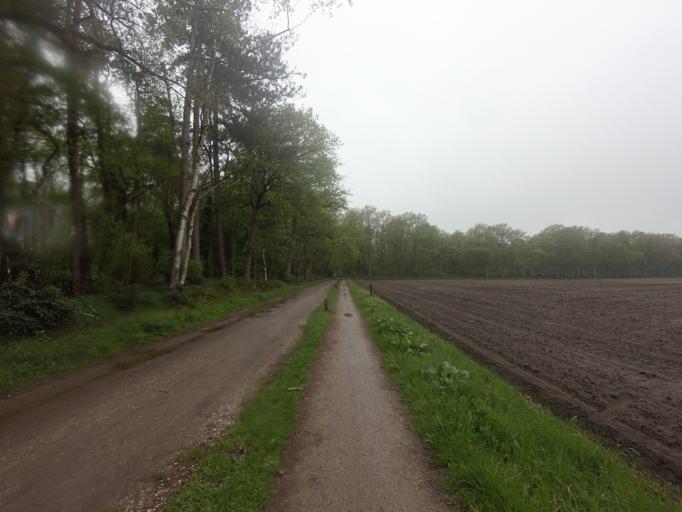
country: NL
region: Overijssel
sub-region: Gemeente Enschede
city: Enschede
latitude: 52.1406
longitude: 6.8634
